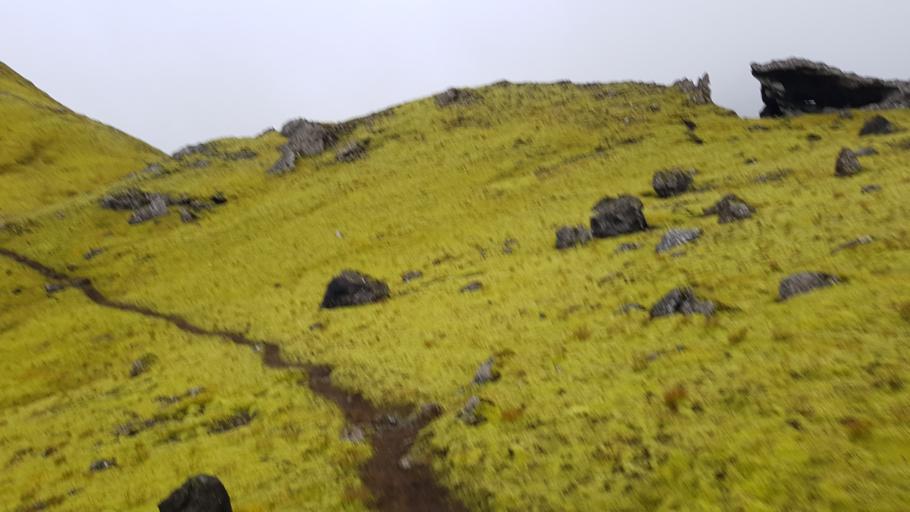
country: IS
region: South
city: Vestmannaeyjar
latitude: 63.5379
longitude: -18.8549
